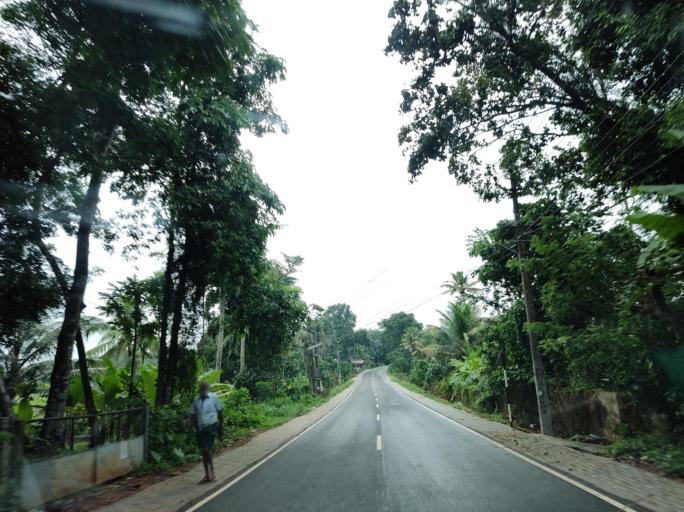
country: IN
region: Kerala
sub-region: Alappuzha
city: Mavelikara
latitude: 9.2275
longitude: 76.5747
